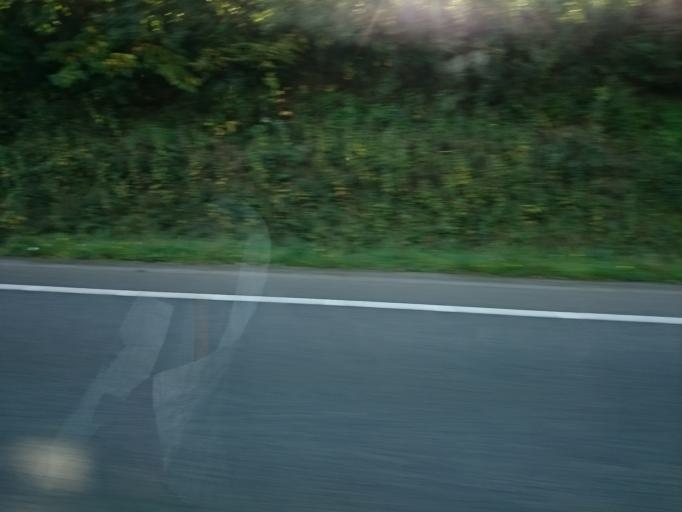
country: FR
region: Brittany
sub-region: Departement des Cotes-d'Armor
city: Graces
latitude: 48.5586
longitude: -3.1815
